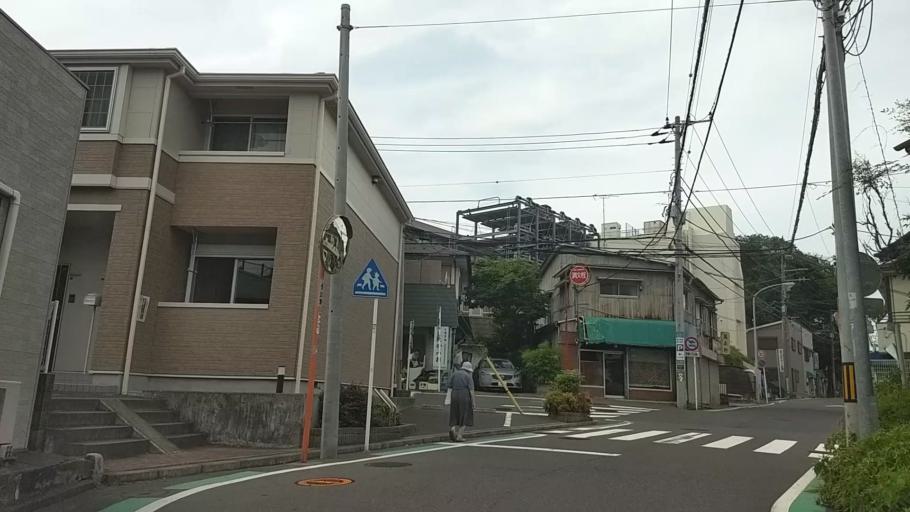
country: JP
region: Kanagawa
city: Yokohama
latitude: 35.4411
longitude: 139.6042
